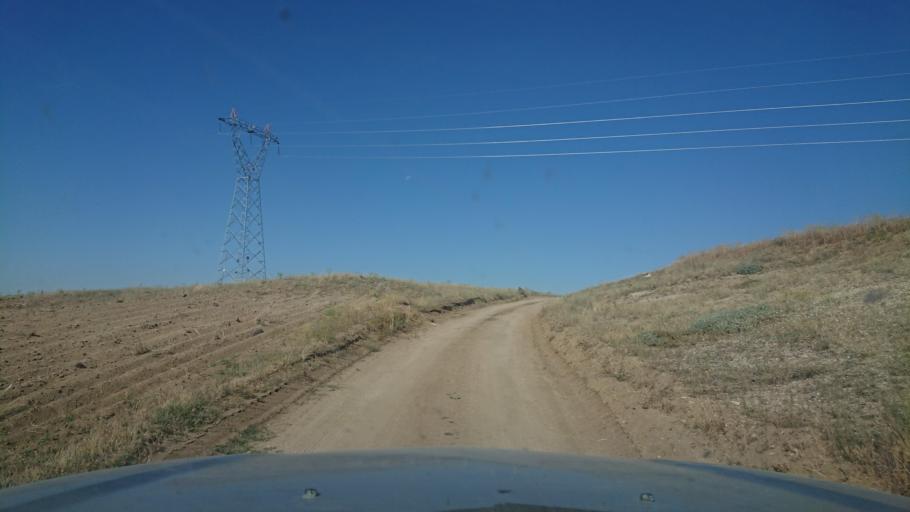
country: TR
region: Aksaray
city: Agacoren
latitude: 38.8345
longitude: 33.9461
